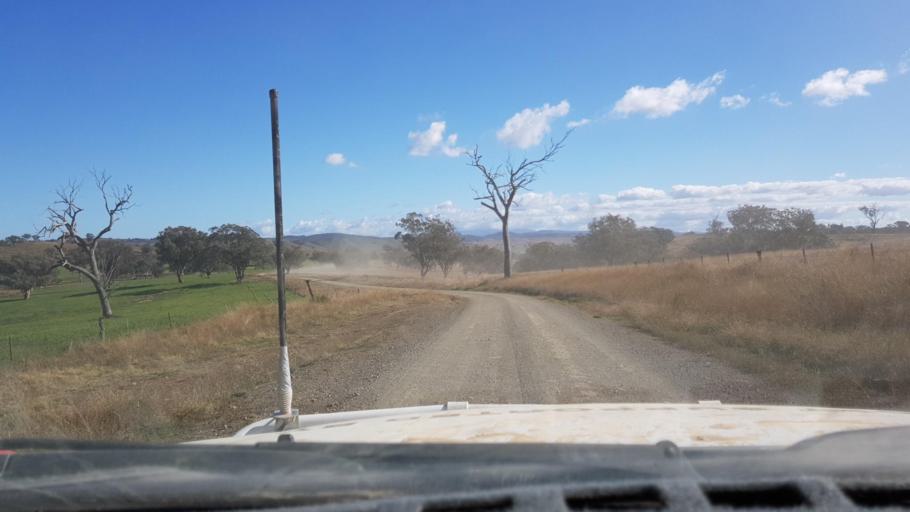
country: AU
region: New South Wales
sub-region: Narrabri
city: Blair Athol
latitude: -30.5493
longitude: 150.4612
